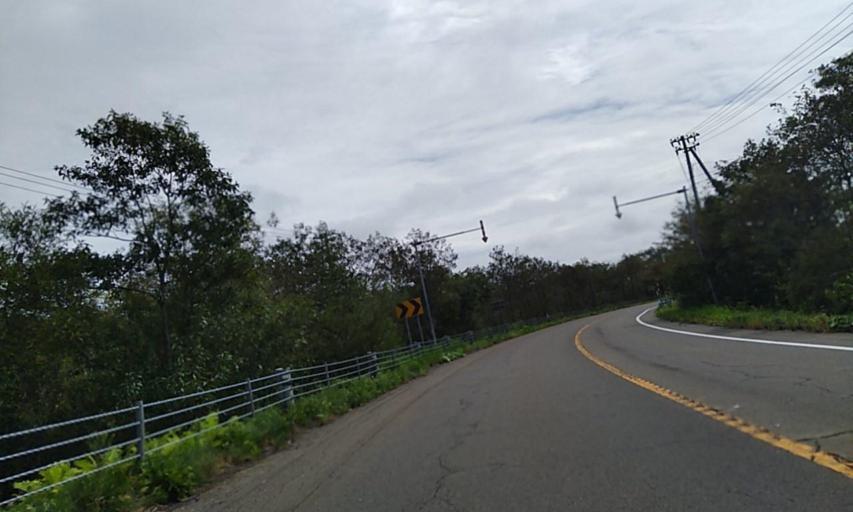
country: JP
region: Hokkaido
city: Shibetsu
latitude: 43.6107
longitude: 145.1854
